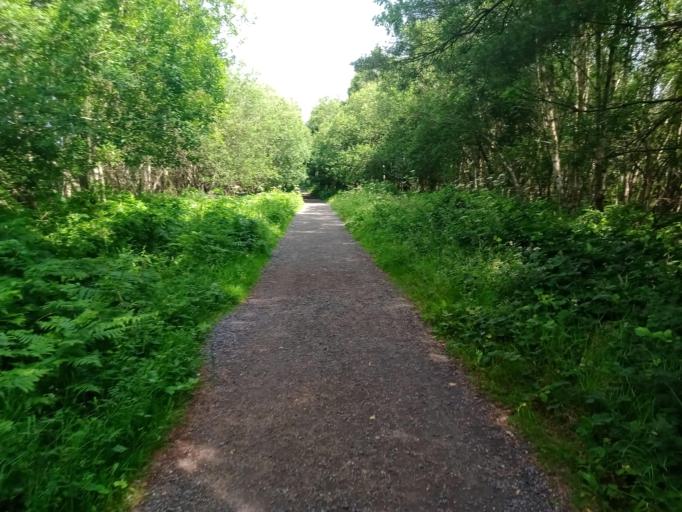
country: IE
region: Leinster
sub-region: Laois
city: Abbeyleix
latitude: 52.8977
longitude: -7.3501
